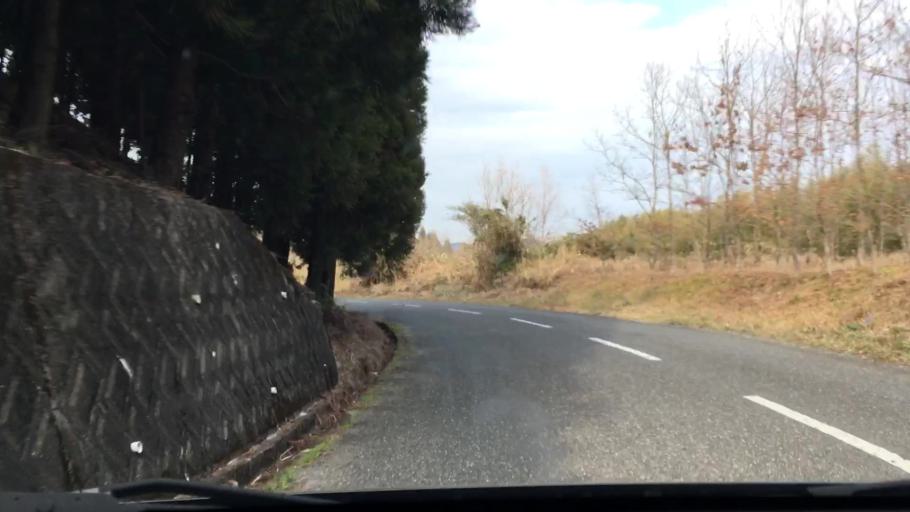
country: JP
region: Miyazaki
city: Nichinan
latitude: 31.6193
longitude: 131.3364
